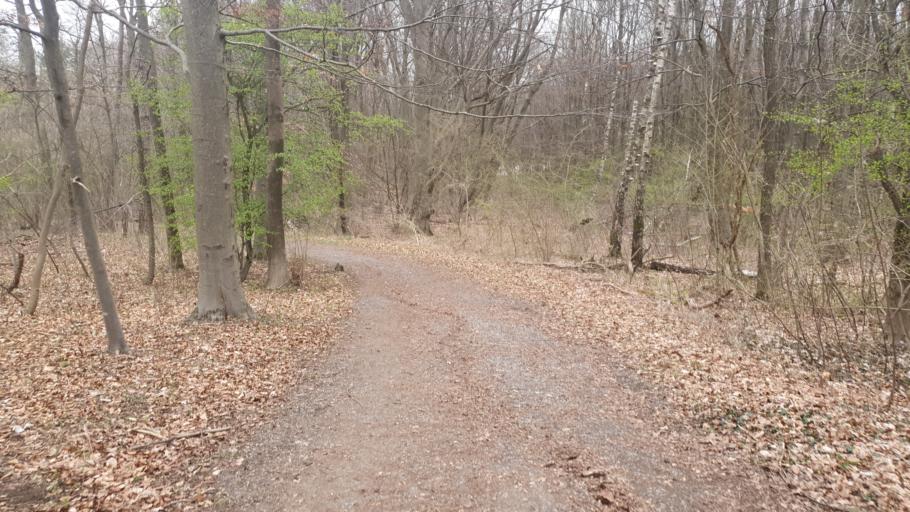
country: DE
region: North Rhine-Westphalia
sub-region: Regierungsbezirk Munster
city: Rheine
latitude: 52.2579
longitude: 7.4399
